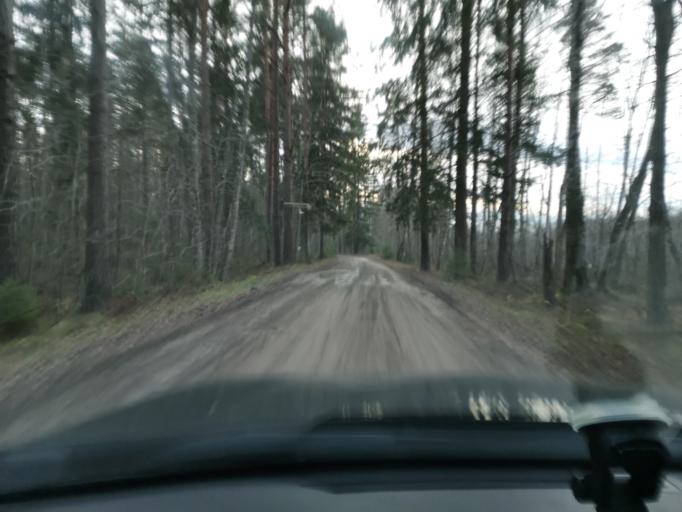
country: EE
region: Ida-Virumaa
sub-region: Sillamaee linn
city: Sillamae
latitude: 59.2566
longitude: 27.9140
